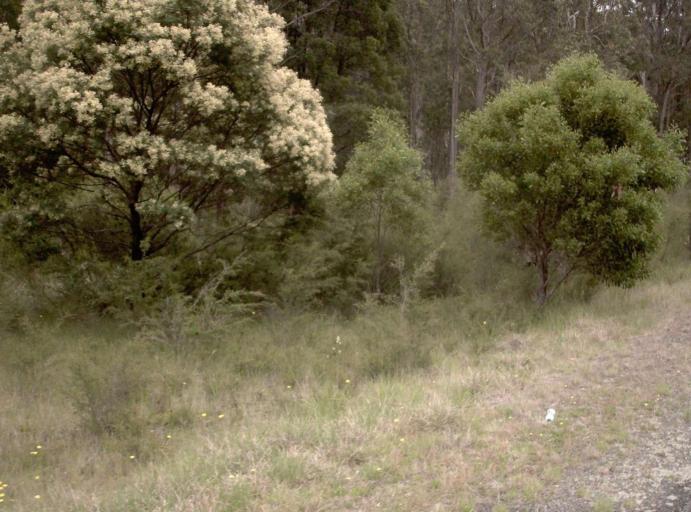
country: AU
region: New South Wales
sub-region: Bombala
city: Bombala
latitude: -37.2354
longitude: 149.2695
